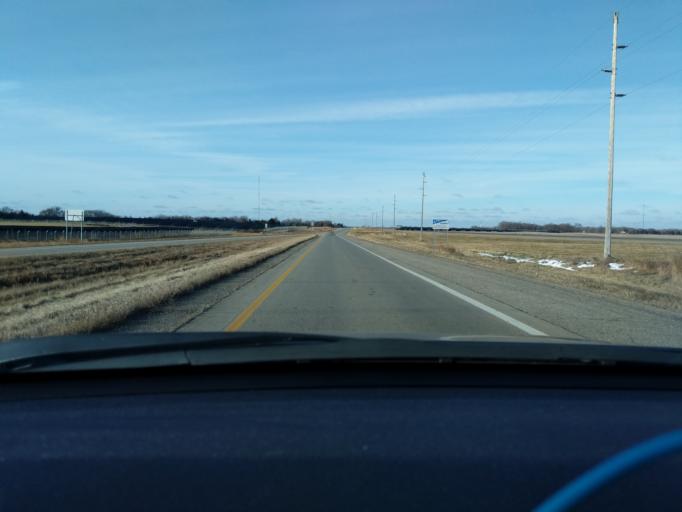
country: US
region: Minnesota
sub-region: Yellow Medicine County
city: Granite Falls
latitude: 44.7964
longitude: -95.4882
